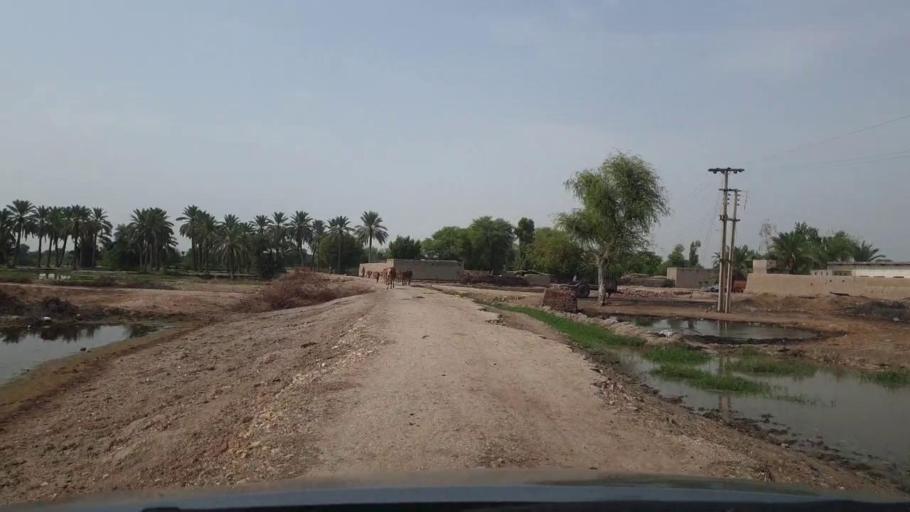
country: PK
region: Sindh
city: Rohri
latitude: 27.6606
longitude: 69.0131
